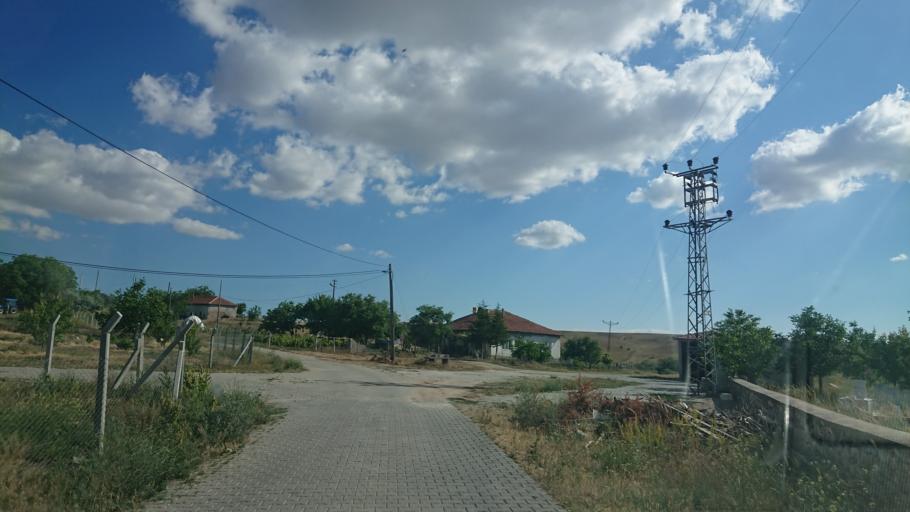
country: TR
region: Aksaray
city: Agacoren
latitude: 38.7528
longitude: 33.8849
